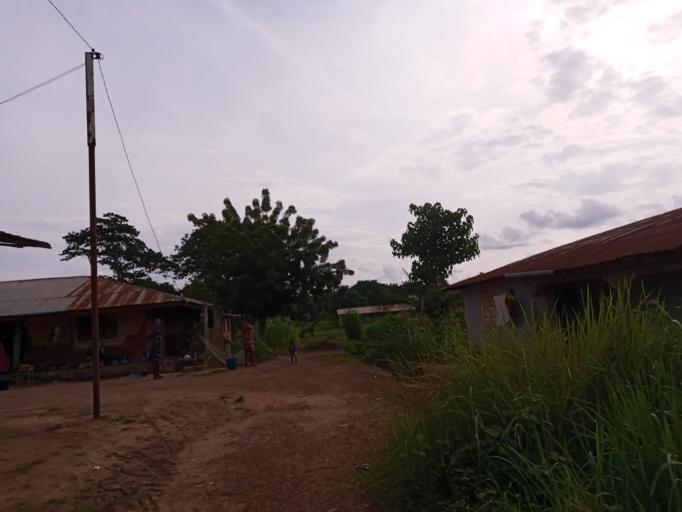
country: SL
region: Northern Province
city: Bumbuna
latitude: 9.0486
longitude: -11.7566
